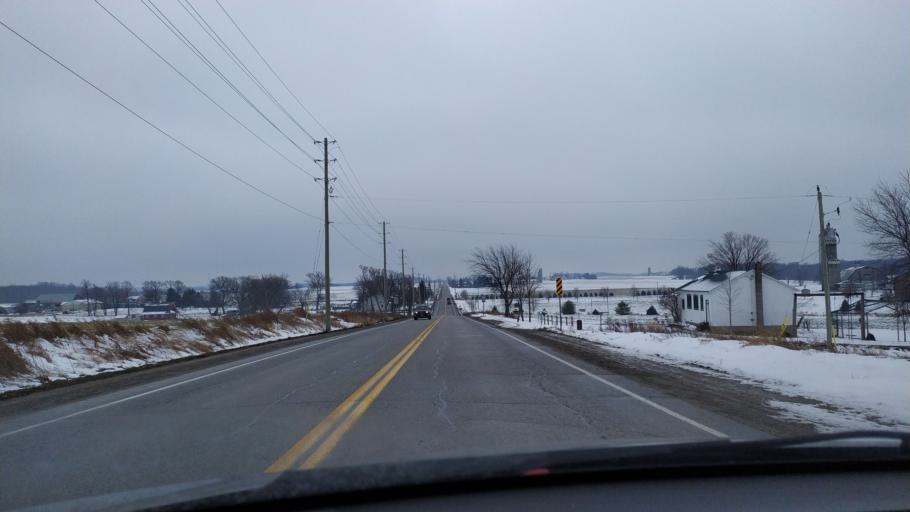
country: CA
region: Ontario
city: Waterloo
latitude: 43.5165
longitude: -80.6200
